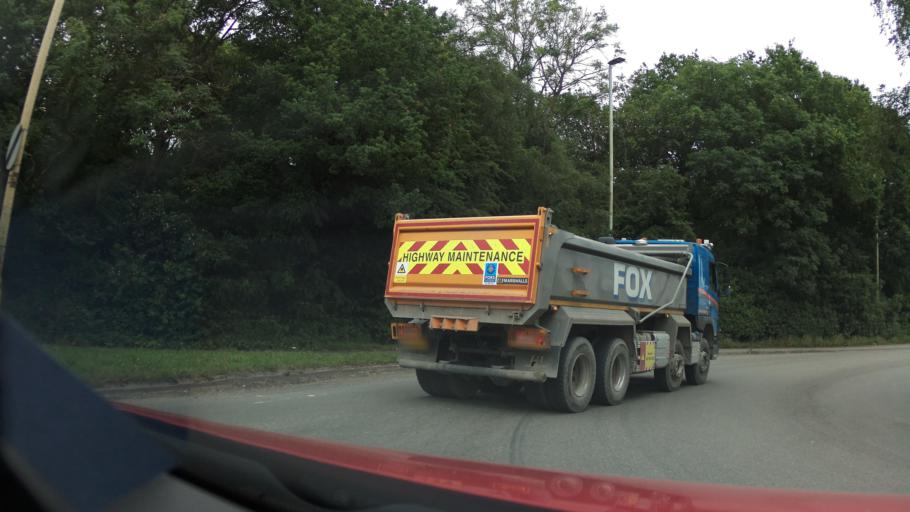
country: GB
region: England
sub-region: Leicestershire
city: Coalville
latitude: 52.7031
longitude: -1.3242
